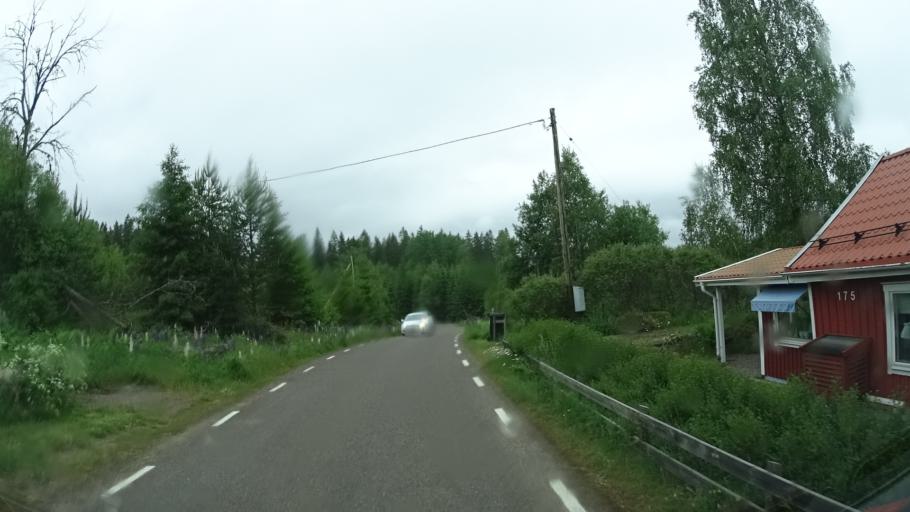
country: SE
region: Kalmar
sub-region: Vimmerby Kommun
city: Sodra Vi
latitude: 57.6959
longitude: 15.7202
